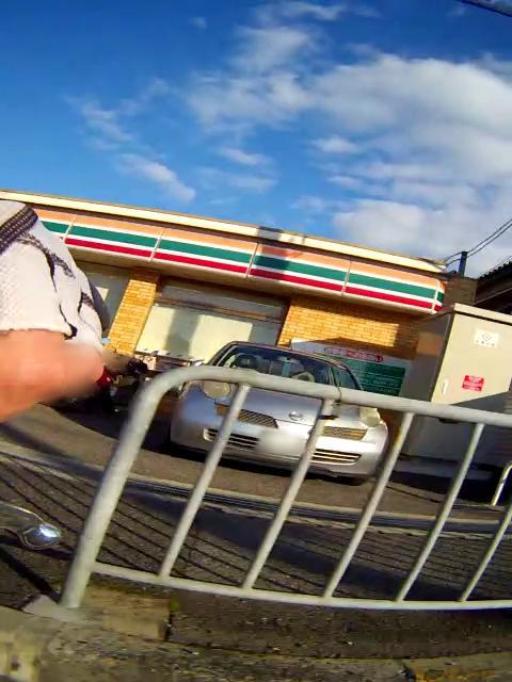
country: JP
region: Hyogo
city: Itami
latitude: 34.7689
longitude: 135.4112
